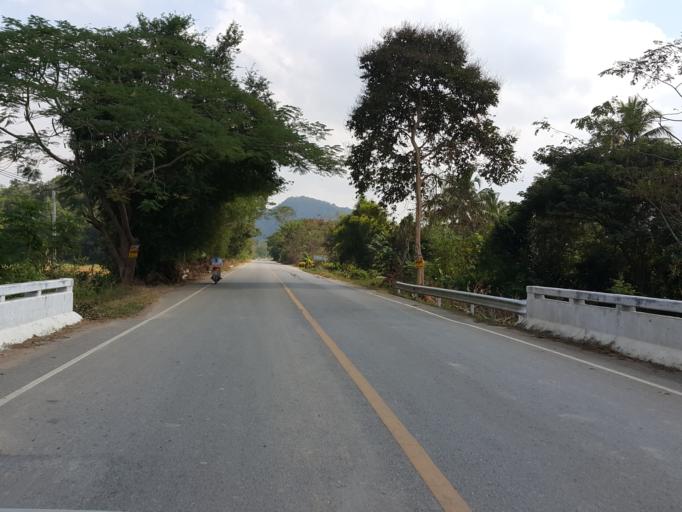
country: TH
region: Sukhothai
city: Thung Saliam
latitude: 17.3351
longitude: 99.4866
